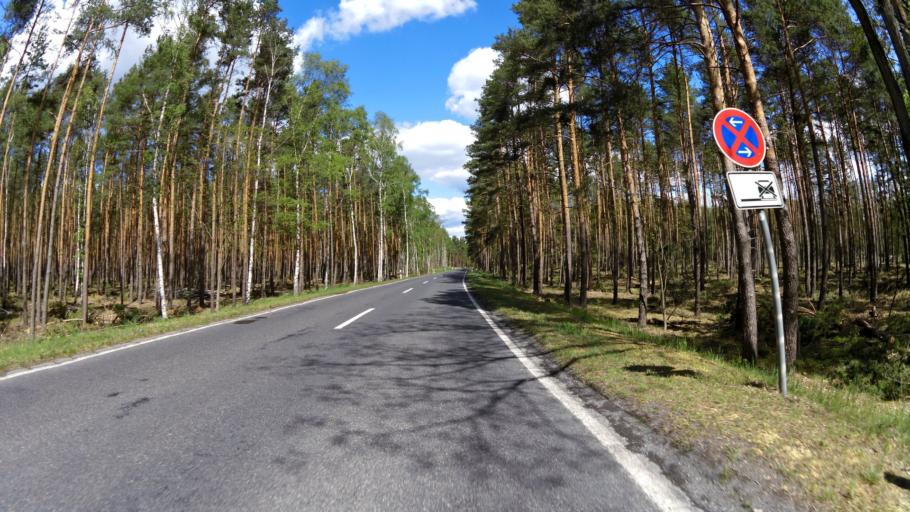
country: DE
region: Brandenburg
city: Wendisch Rietz
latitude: 52.1418
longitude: 13.9668
